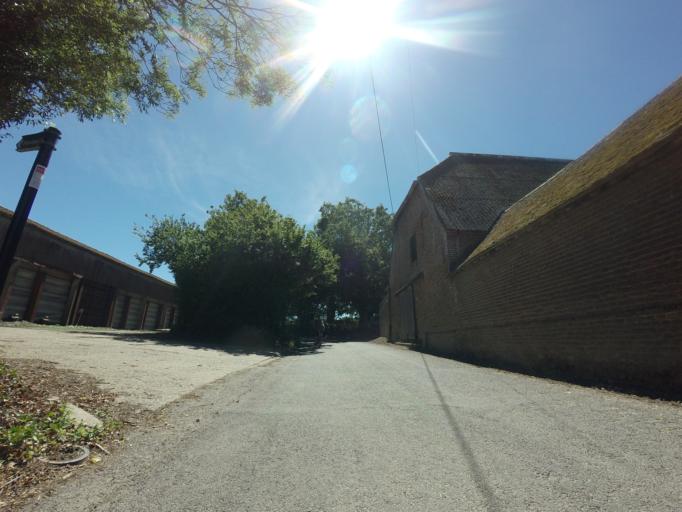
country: GB
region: England
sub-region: Kent
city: Deal
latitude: 51.1959
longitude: 1.3626
